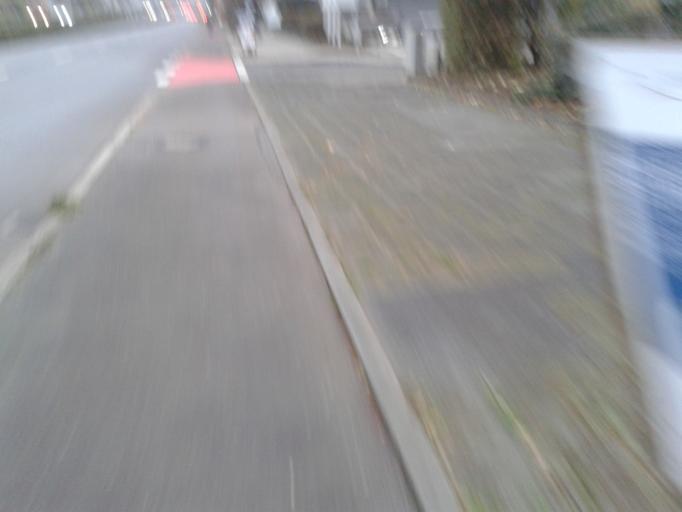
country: DE
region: Baden-Wuerttemberg
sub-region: Karlsruhe Region
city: Heidelberg
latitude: 49.4140
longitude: 8.6768
